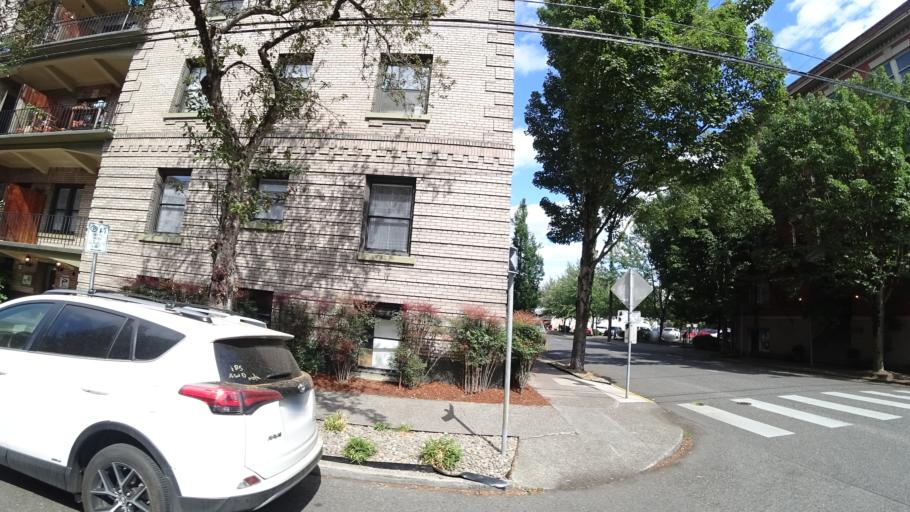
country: US
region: Oregon
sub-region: Multnomah County
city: Portland
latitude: 45.5263
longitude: -122.6964
